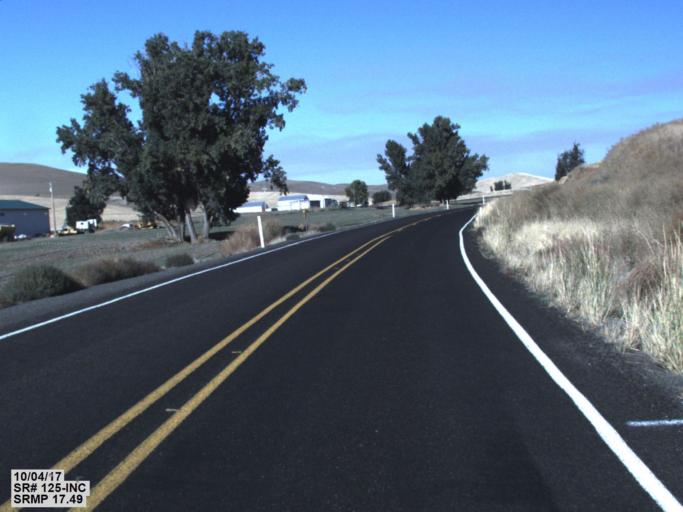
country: US
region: Washington
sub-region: Walla Walla County
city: Walla Walla
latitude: 46.2198
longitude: -118.3919
